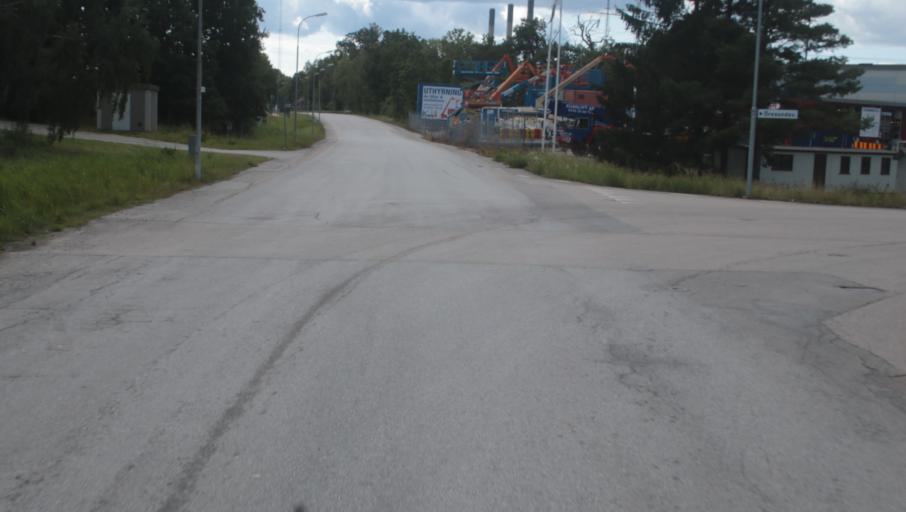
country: SE
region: Blekinge
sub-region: Karlshamns Kommun
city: Karlshamn
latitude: 56.1629
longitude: 14.8444
